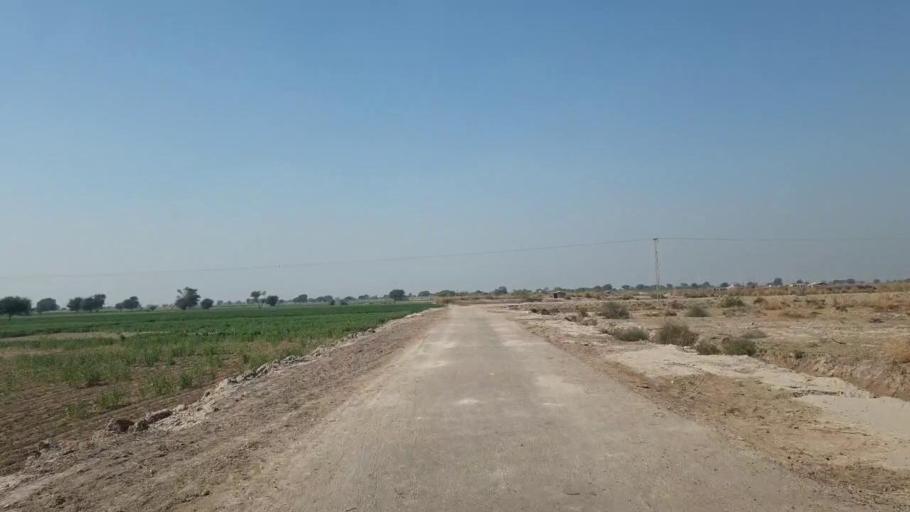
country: PK
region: Sindh
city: Shahpur Chakar
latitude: 26.1225
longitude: 68.6058
